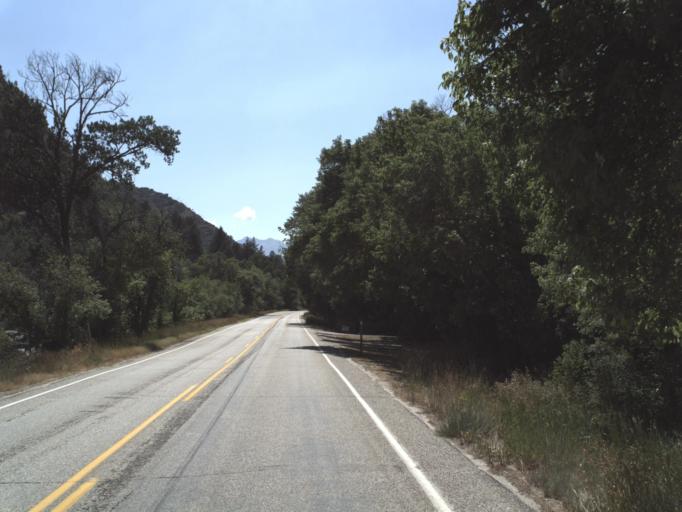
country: US
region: Utah
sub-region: Weber County
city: Wolf Creek
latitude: 41.2709
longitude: -111.6661
